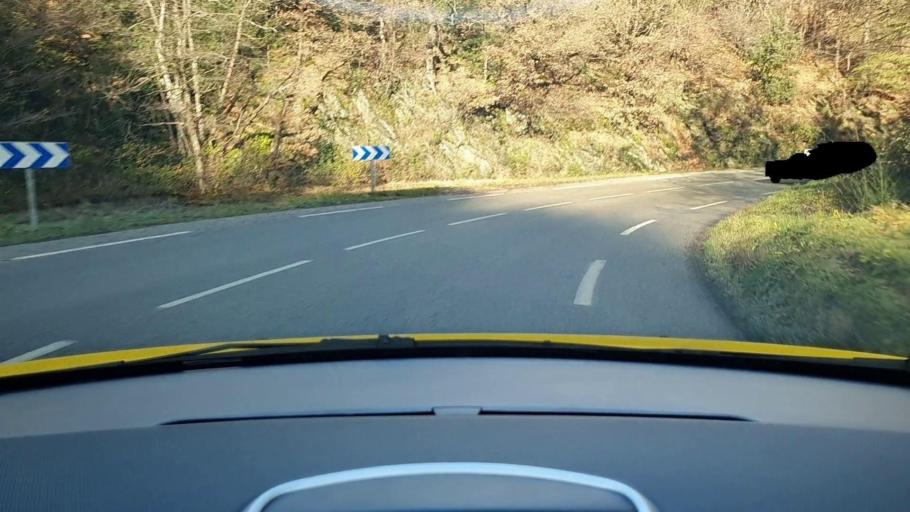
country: FR
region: Languedoc-Roussillon
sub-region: Departement du Gard
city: Branoux-les-Taillades
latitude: 44.3722
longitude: 3.9419
